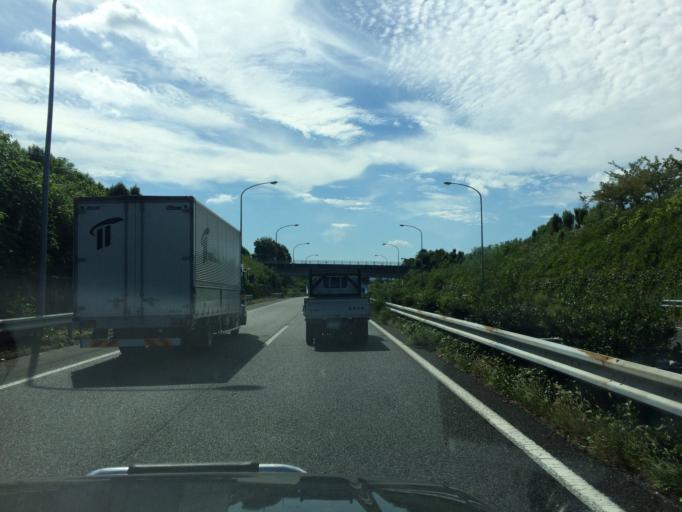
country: JP
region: Osaka
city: Izumi
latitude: 34.4859
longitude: 135.4654
